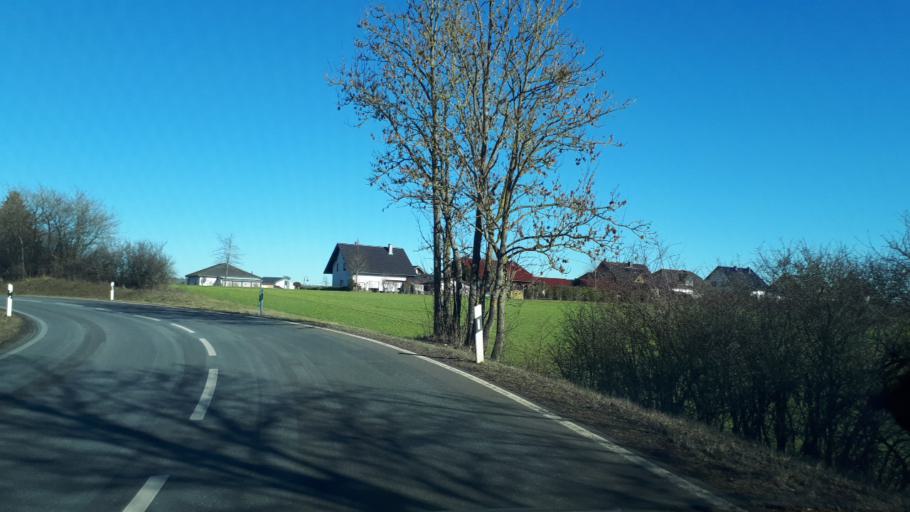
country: DE
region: Rheinland-Pfalz
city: Strohn
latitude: 50.1067
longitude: 6.9173
